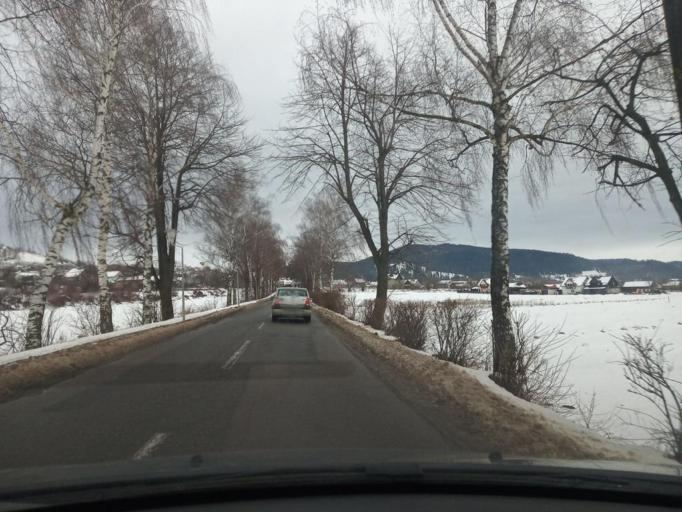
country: RO
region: Suceava
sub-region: Oras Gura Humorului
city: Gura Humorului
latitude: 47.5454
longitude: 25.8711
